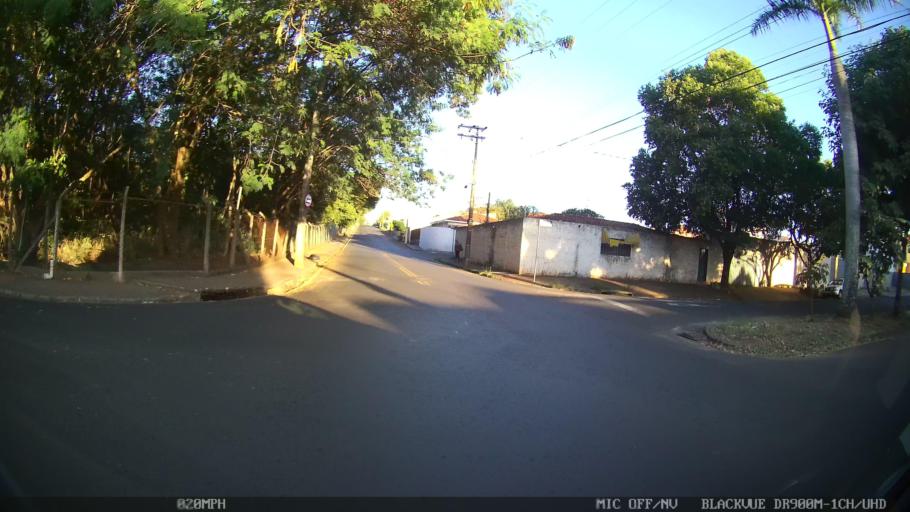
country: BR
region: Sao Paulo
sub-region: Sao Jose Do Rio Preto
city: Sao Jose do Rio Preto
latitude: -20.7784
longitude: -49.3571
